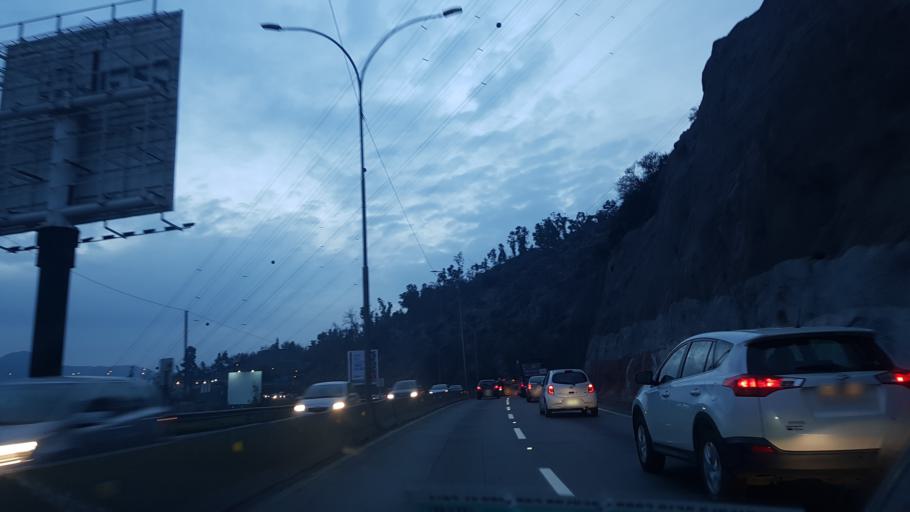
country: CL
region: Santiago Metropolitan
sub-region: Provincia de Santiago
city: Villa Presidente Frei, Nunoa, Santiago, Chile
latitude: -33.3911
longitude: -70.6061
